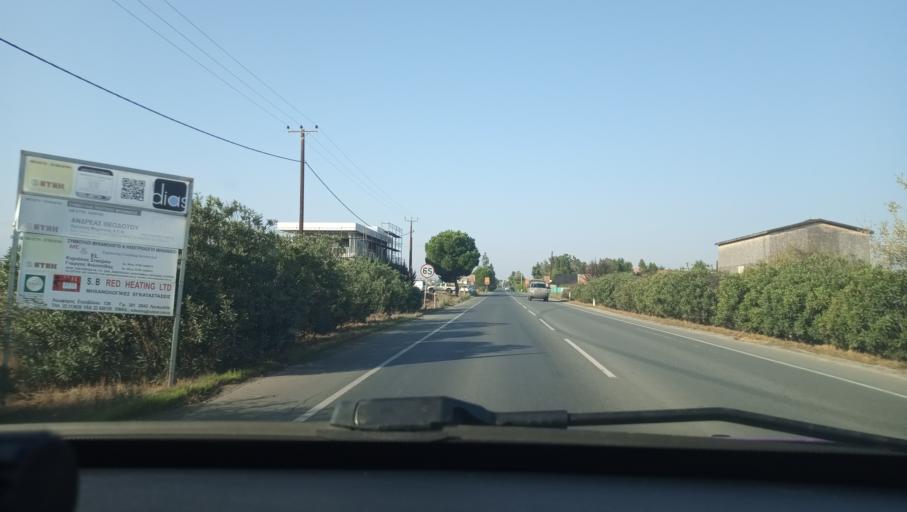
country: CY
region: Lefkosia
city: Kato Deftera
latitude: 35.0910
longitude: 33.2756
